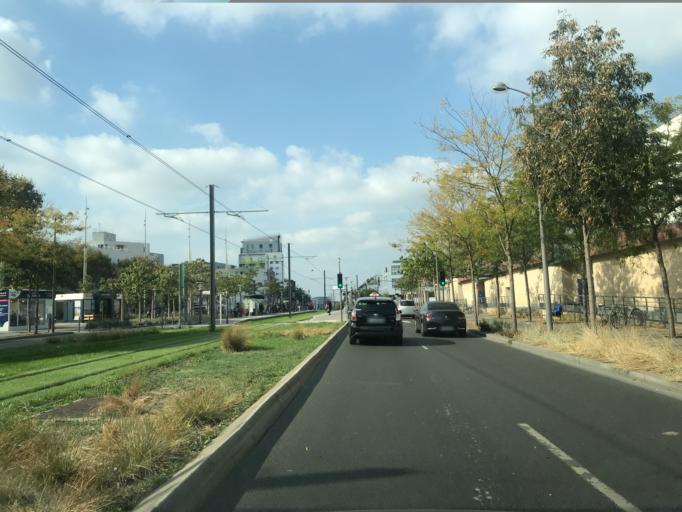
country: FR
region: Ile-de-France
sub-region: Departement des Hauts-de-Seine
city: La Garenne-Colombes
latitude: 48.9133
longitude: 2.2306
